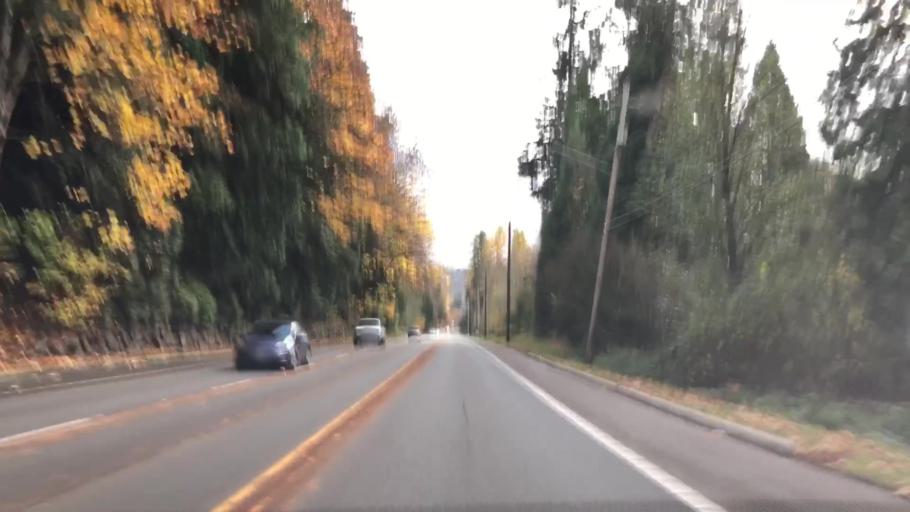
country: US
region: Washington
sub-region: King County
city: Woodinville
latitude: 47.7614
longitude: -122.1463
